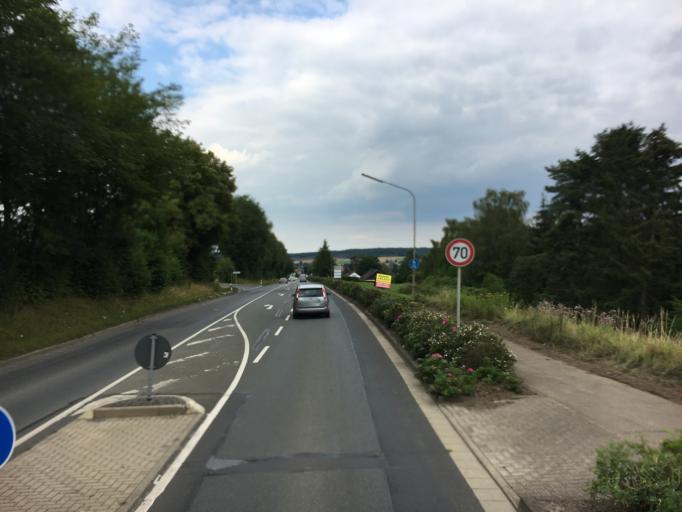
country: DE
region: Hesse
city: Neustadt (Hessen)
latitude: 50.8483
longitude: 9.1000
